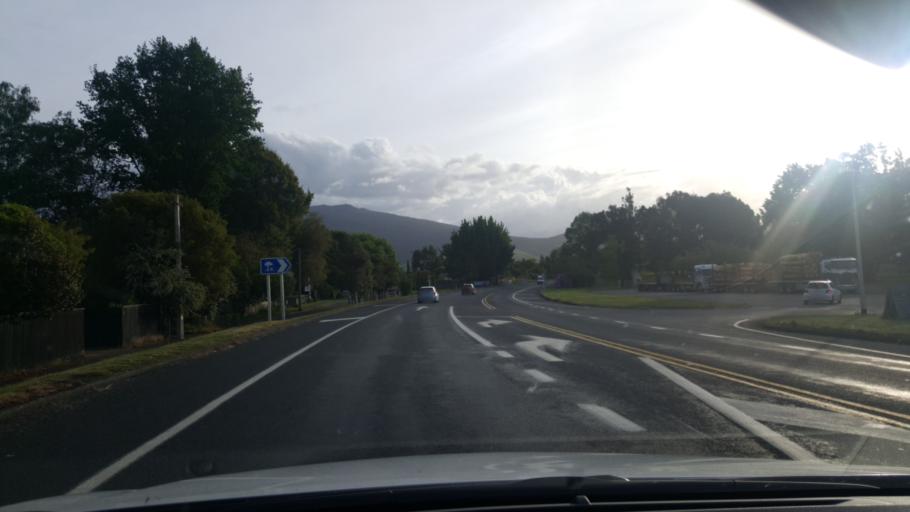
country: NZ
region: Waikato
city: Turangi
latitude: -38.9870
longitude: 175.8182
